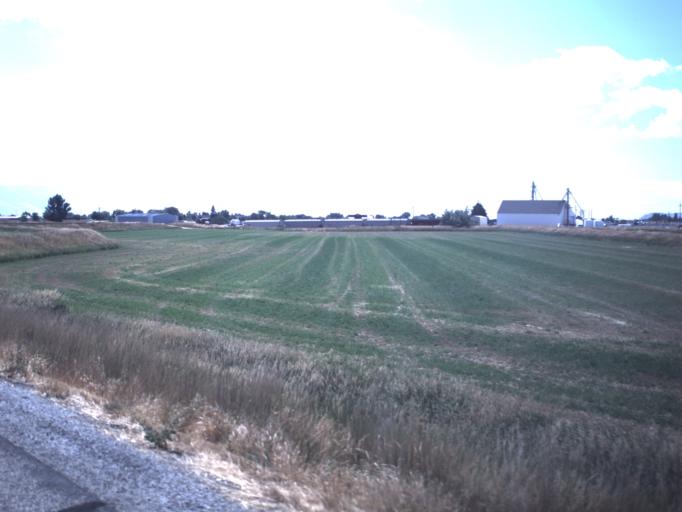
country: US
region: Utah
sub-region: Box Elder County
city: Garland
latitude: 41.7458
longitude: -112.1463
